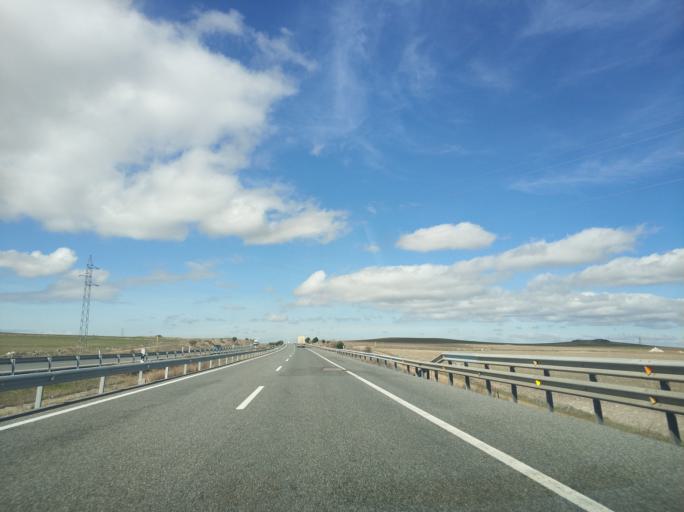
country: ES
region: Castille and Leon
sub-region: Provincia de Burgos
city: Albillos
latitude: 42.3068
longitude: -3.7902
